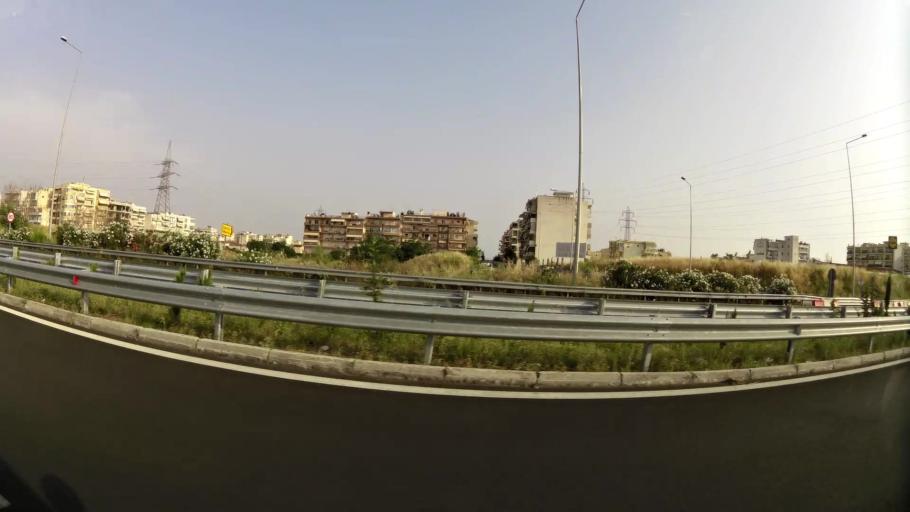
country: GR
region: Central Macedonia
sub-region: Nomos Thessalonikis
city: Evosmos
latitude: 40.6785
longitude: 22.9013
